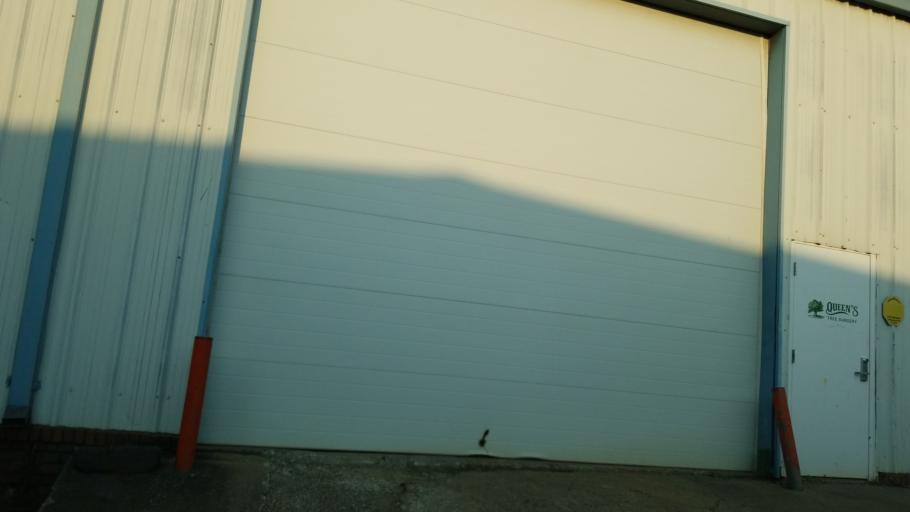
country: US
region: Tennessee
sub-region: Davidson County
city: Nashville
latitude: 36.1386
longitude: -86.7721
